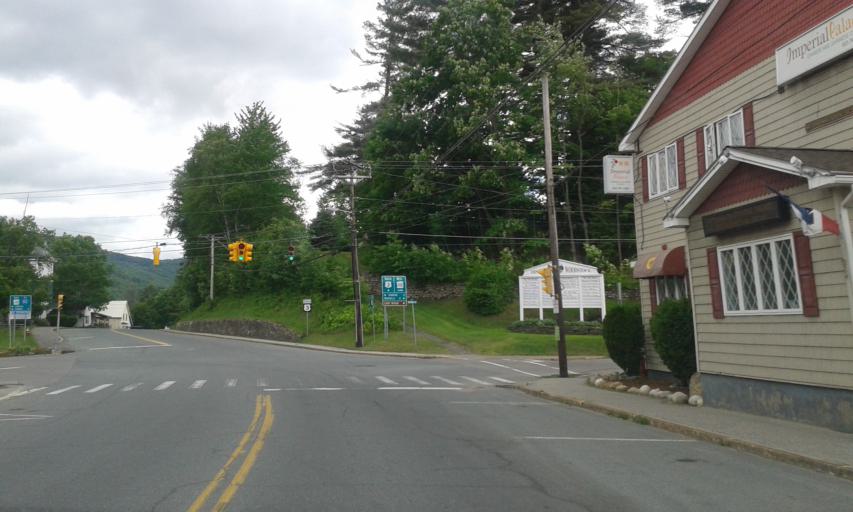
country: US
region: New Hampshire
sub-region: Grafton County
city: Woodstock
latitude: 44.0308
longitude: -71.6867
